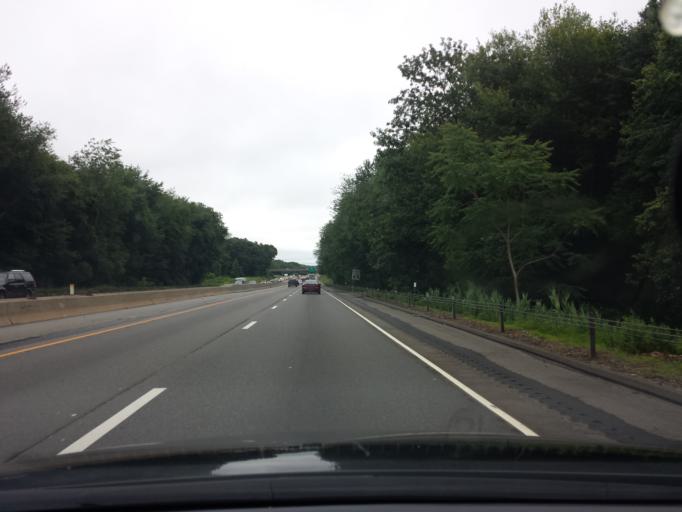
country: US
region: Connecticut
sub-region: New Haven County
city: Madison Center
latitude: 41.2884
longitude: -72.6319
